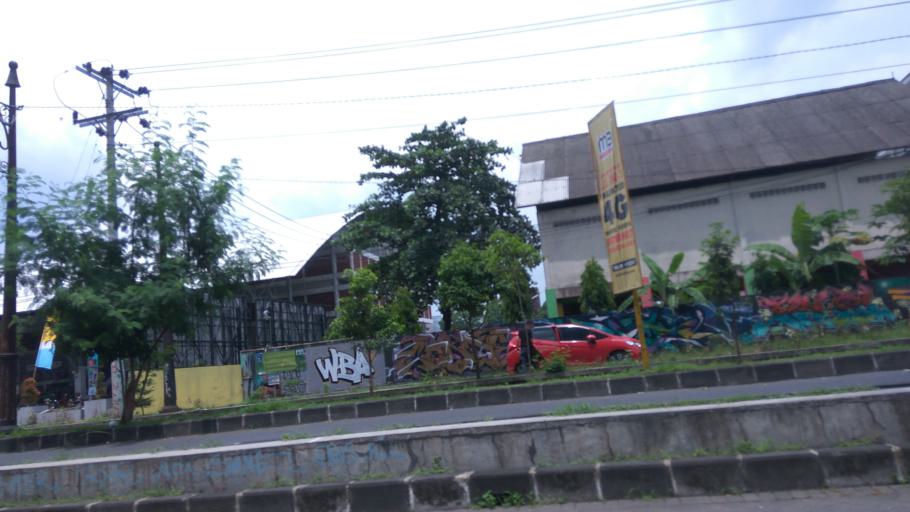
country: ID
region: Daerah Istimewa Yogyakarta
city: Yogyakarta
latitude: -7.7677
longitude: 110.3866
